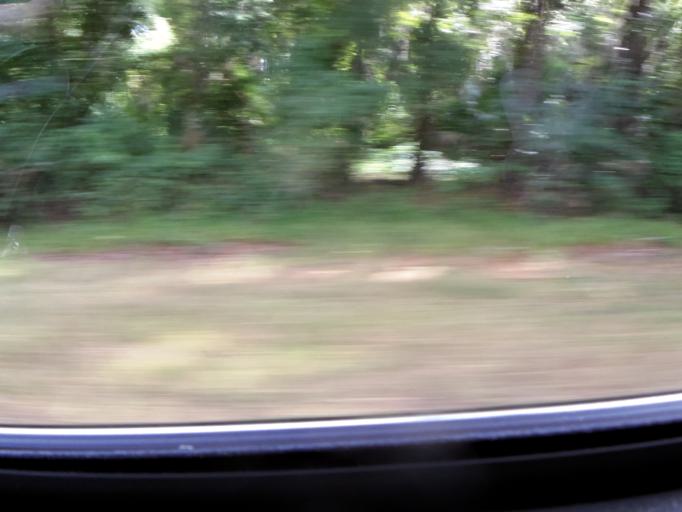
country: US
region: Georgia
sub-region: Glynn County
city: Dock Junction
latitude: 31.1637
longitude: -81.5581
